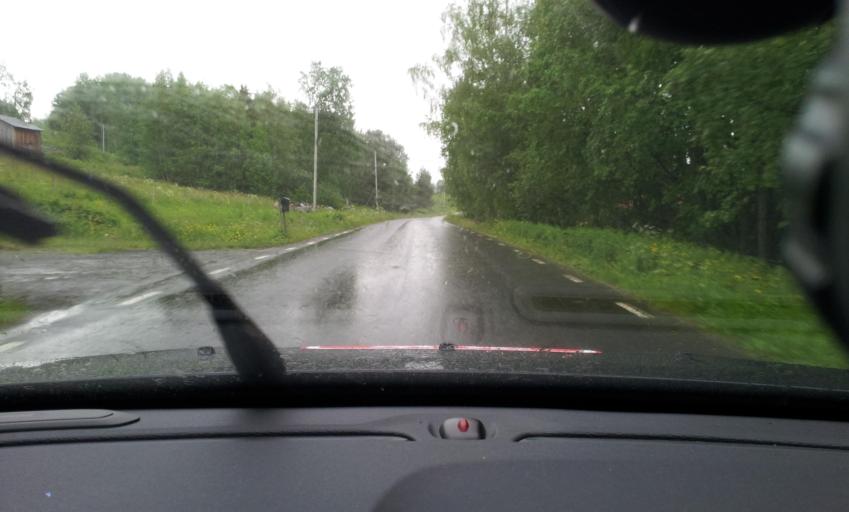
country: SE
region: Jaemtland
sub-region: Are Kommun
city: Are
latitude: 63.3133
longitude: 13.1833
